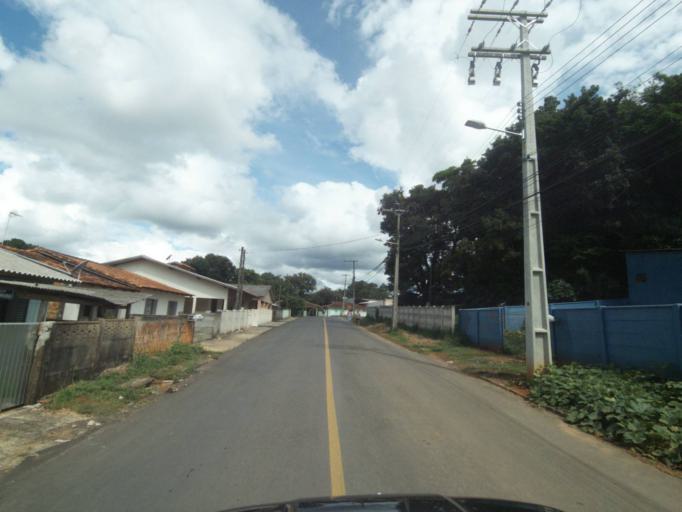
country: BR
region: Parana
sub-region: Telemaco Borba
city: Telemaco Borba
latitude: -24.3162
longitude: -50.6304
